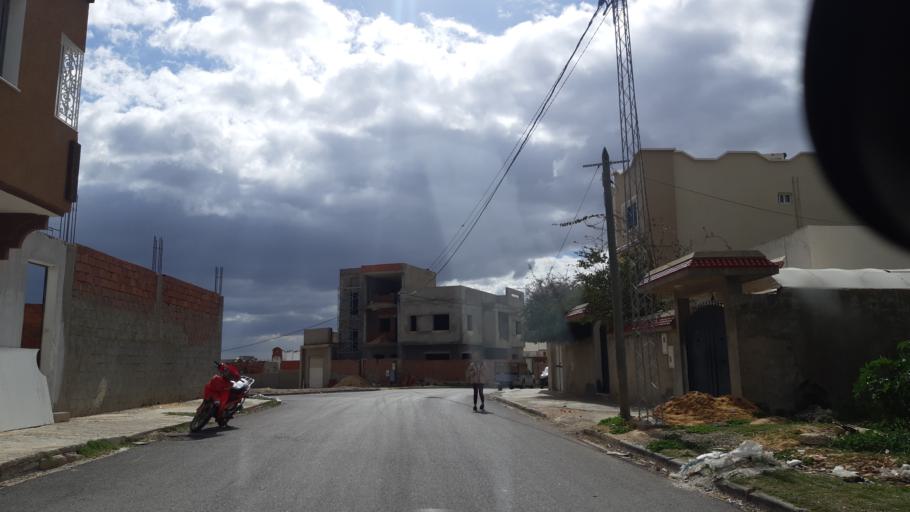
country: TN
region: Susah
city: Akouda
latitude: 35.8706
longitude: 10.5192
